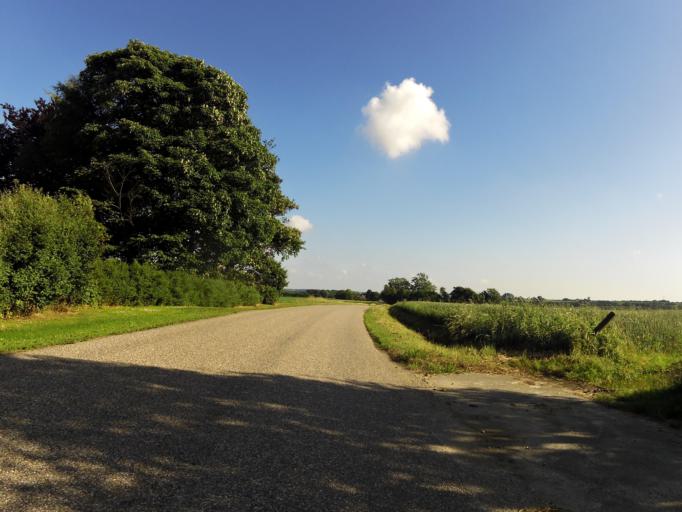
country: DK
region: South Denmark
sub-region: Vejen Kommune
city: Rodding
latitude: 55.3227
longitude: 9.1811
